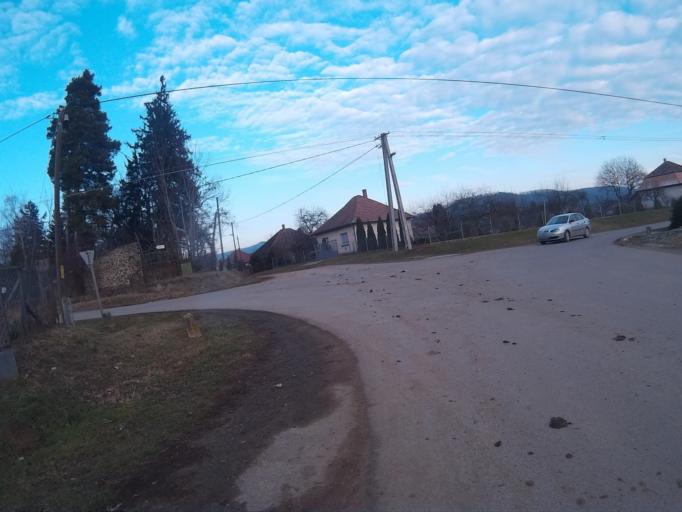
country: HU
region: Nograd
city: Bercel
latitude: 47.9809
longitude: 19.4234
